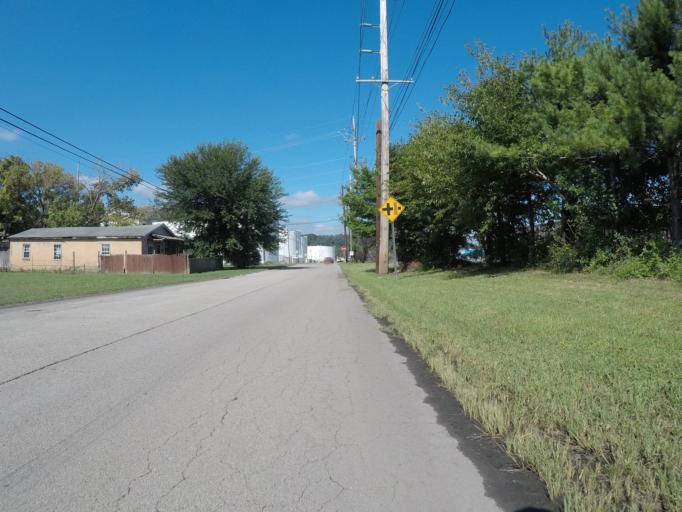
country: US
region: West Virginia
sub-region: Wayne County
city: Kenova
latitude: 38.4057
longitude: -82.5856
